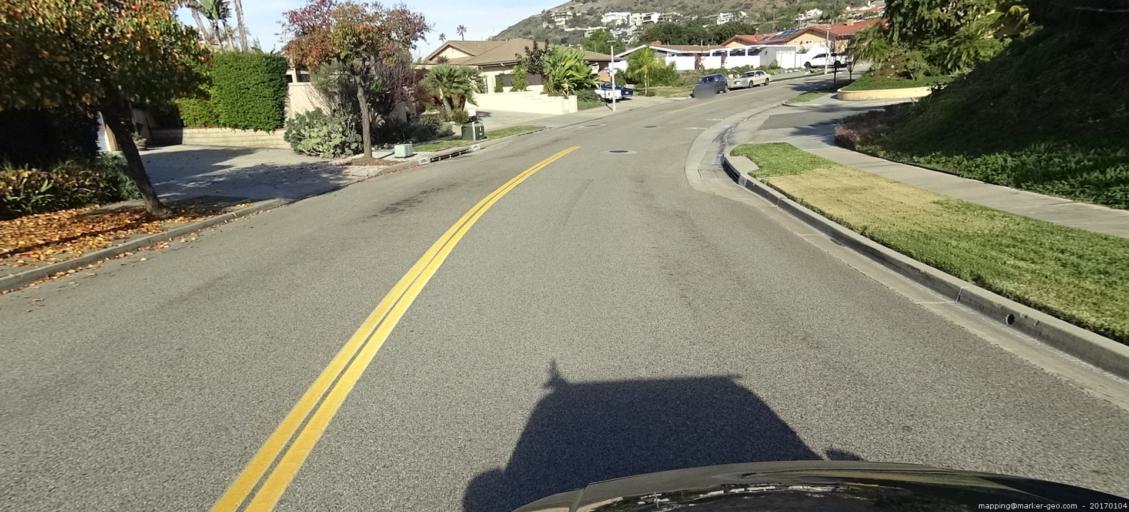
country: US
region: California
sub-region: Orange County
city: Dana Point
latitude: 33.4895
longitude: -117.7292
